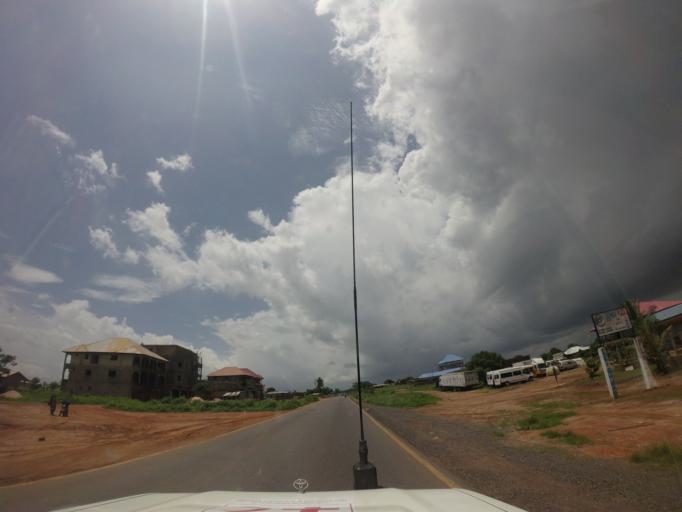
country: SL
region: Western Area
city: Waterloo
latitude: 8.3356
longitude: -13.0321
